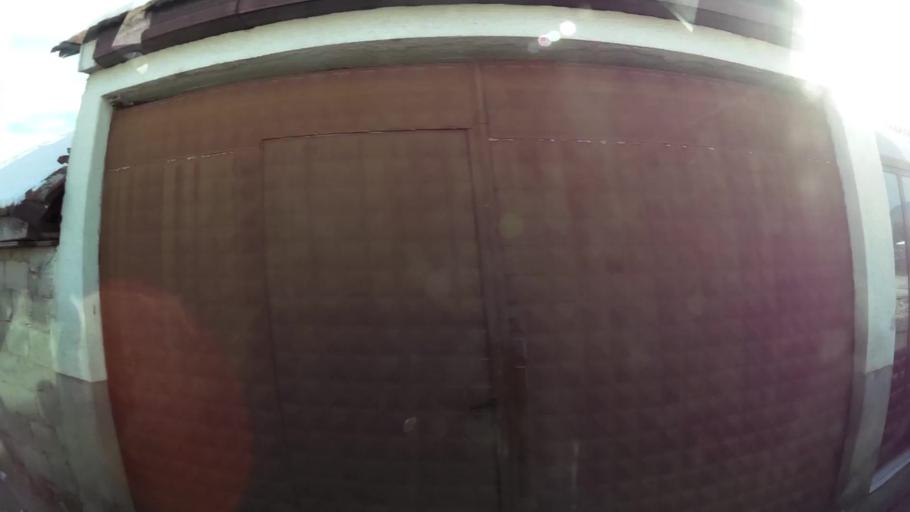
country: MK
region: Saraj
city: Saraj
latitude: 41.9985
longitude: 21.3188
